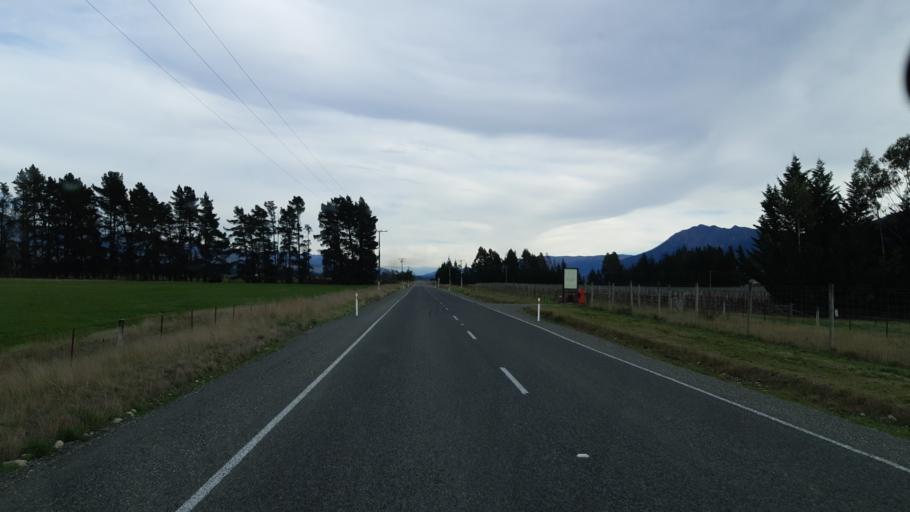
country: NZ
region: Tasman
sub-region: Tasman District
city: Richmond
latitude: -41.6036
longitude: 173.4163
